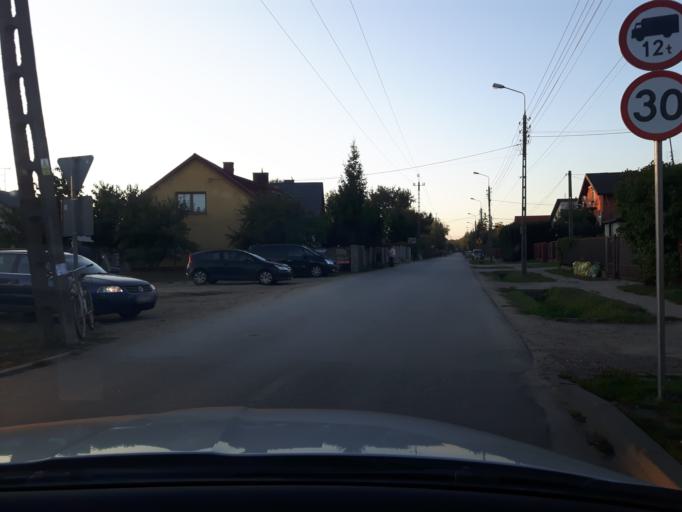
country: PL
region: Masovian Voivodeship
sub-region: Powiat wolominski
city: Kobylka
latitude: 52.3380
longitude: 21.1818
